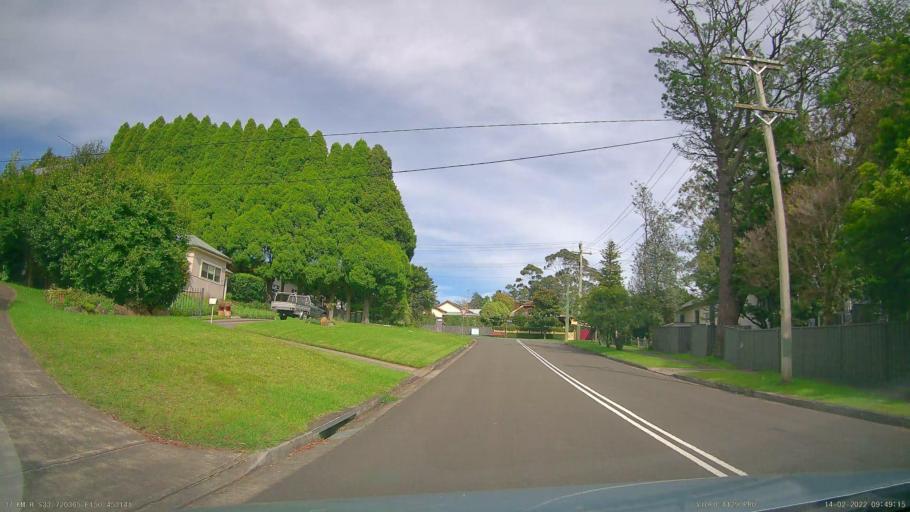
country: AU
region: New South Wales
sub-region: Blue Mountains Municipality
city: Hazelbrook
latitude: -33.7199
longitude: 150.4528
